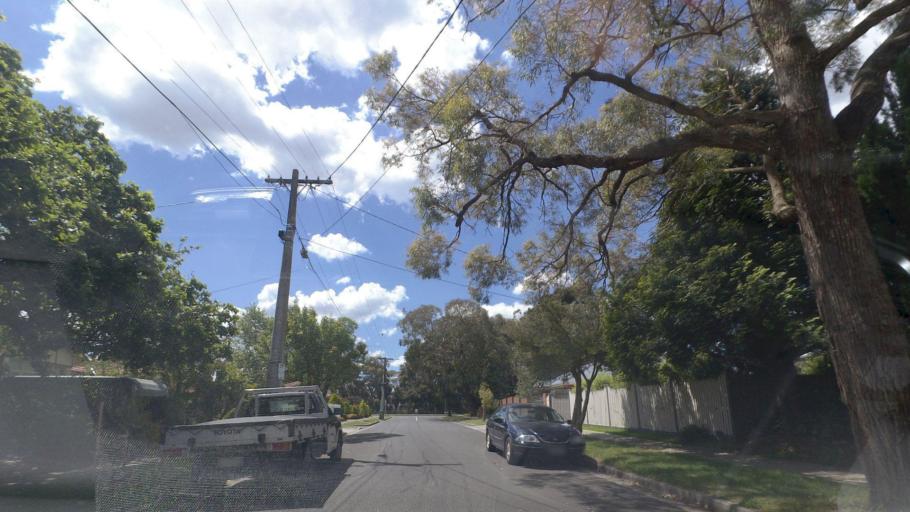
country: AU
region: Victoria
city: Mitcham
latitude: -37.8180
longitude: 145.2101
